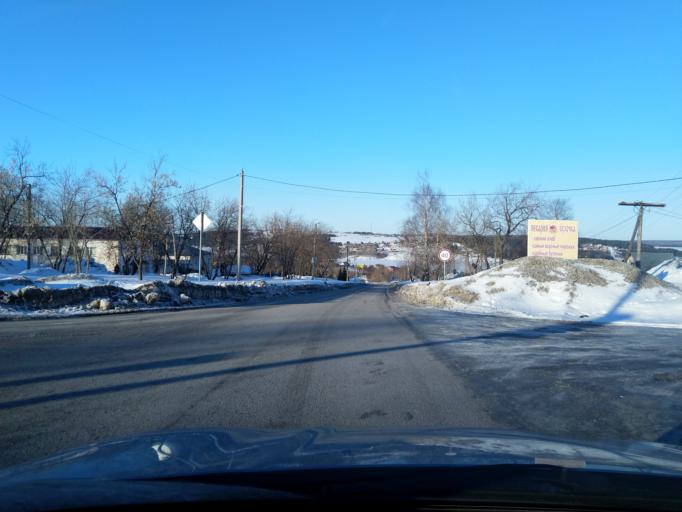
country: RU
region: Perm
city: Polazna
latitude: 58.2912
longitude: 56.4143
